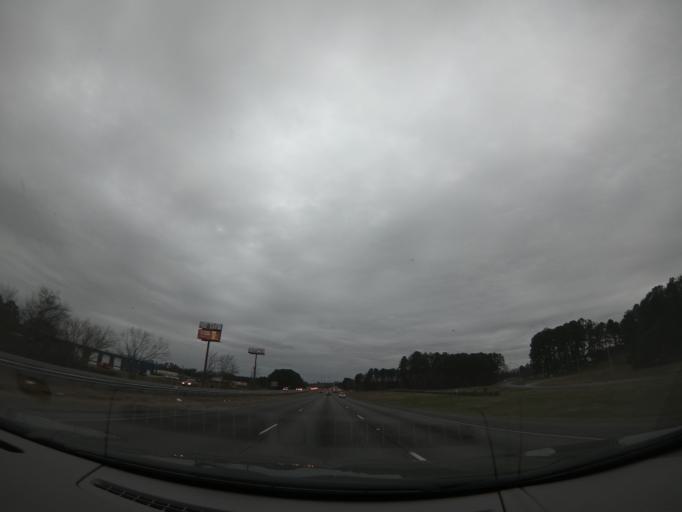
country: US
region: Georgia
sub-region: Gordon County
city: Calhoun
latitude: 34.5662
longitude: -84.9433
